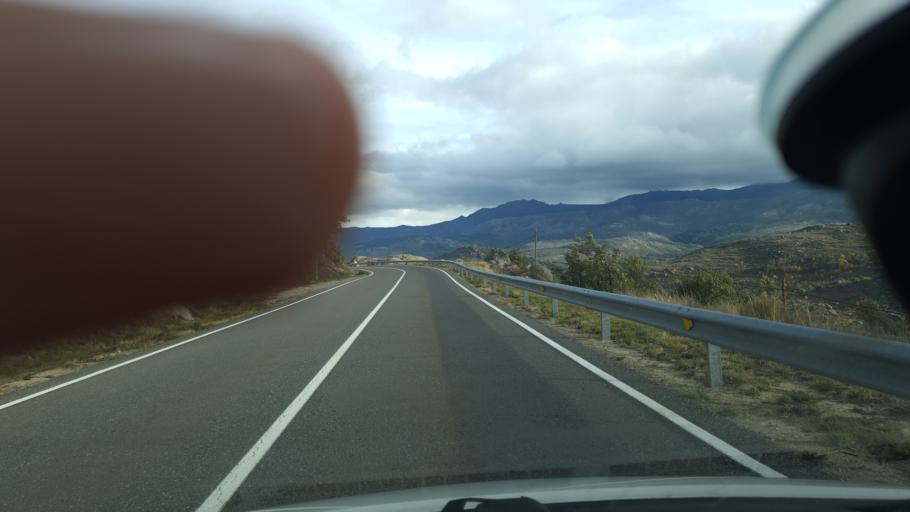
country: ES
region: Castille and Leon
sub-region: Provincia de Avila
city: Navalosa
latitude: 40.3945
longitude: -4.9159
